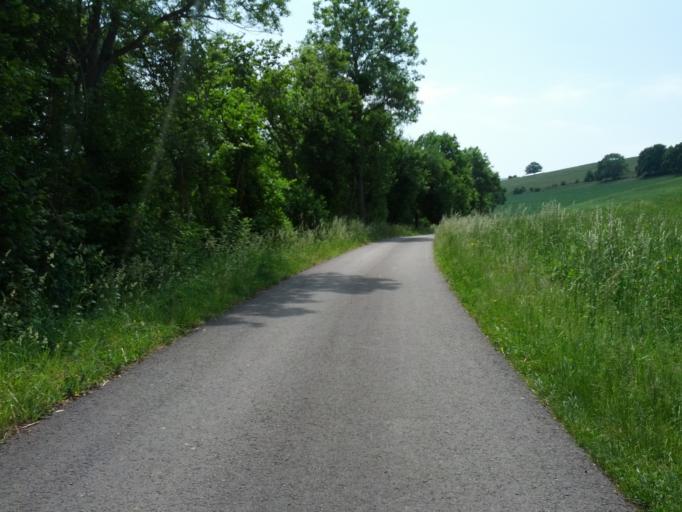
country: DE
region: Thuringia
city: Wiesenthal
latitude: 50.7197
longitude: 10.1636
